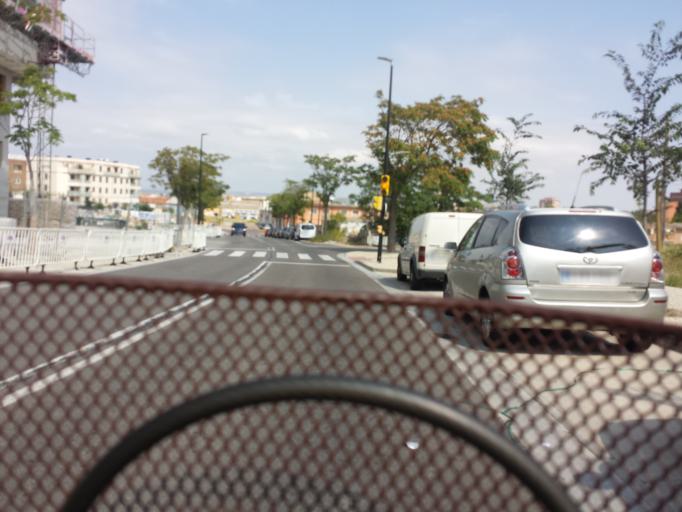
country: ES
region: Aragon
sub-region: Provincia de Zaragoza
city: Oliver-Valdefierro, Oliver, Valdefierro
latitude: 41.6396
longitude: -0.9252
